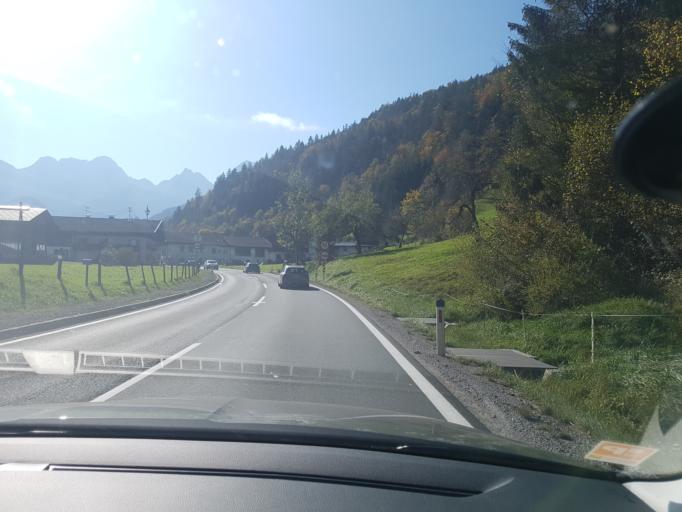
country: AT
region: Salzburg
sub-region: Politischer Bezirk Zell am See
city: Unken
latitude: 47.6171
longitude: 12.7072
